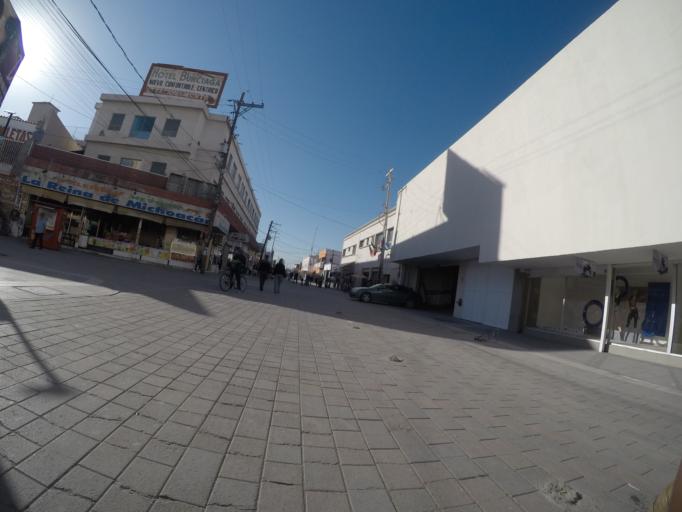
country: MX
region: Chihuahua
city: Ciudad Juarez
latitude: 31.7398
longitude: -106.4862
